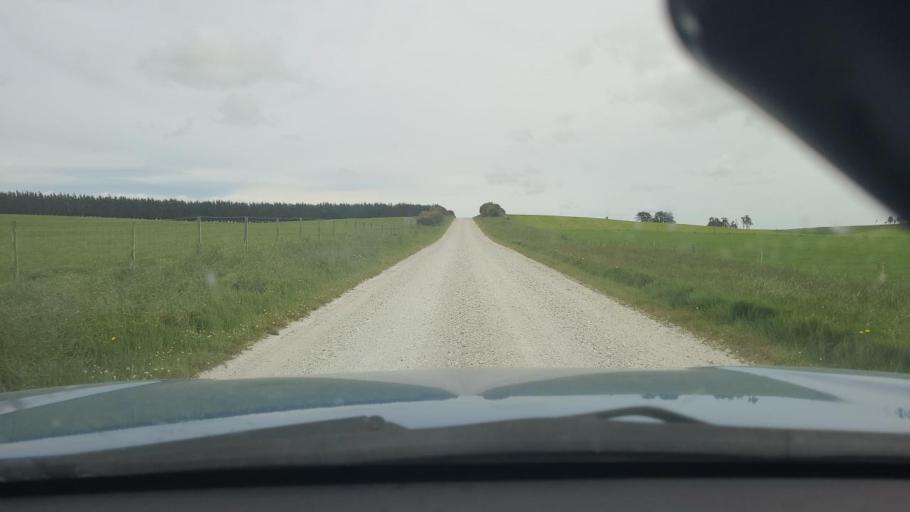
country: NZ
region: Southland
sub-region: Invercargill City
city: Invercargill
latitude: -46.4887
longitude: 168.6874
